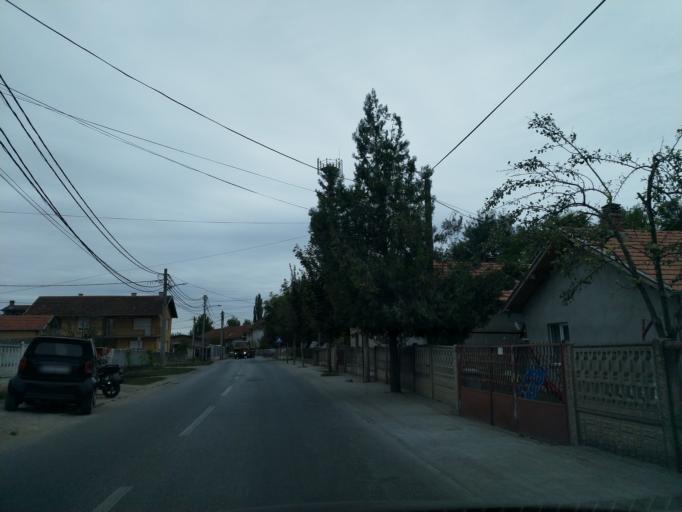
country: RS
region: Central Serbia
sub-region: Pomoravski Okrug
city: Paracin
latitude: 43.8554
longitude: 21.3975
